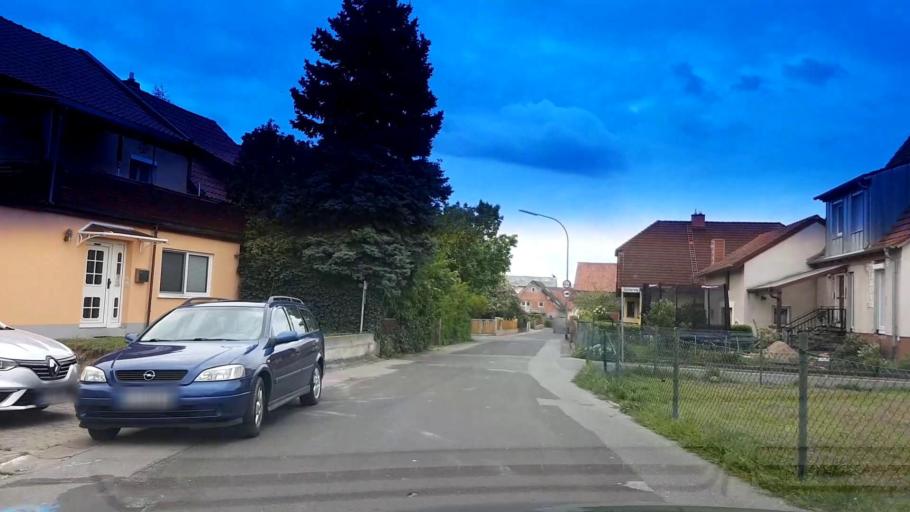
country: DE
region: Bavaria
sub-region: Upper Franconia
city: Oberhaid
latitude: 49.9341
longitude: 10.8137
